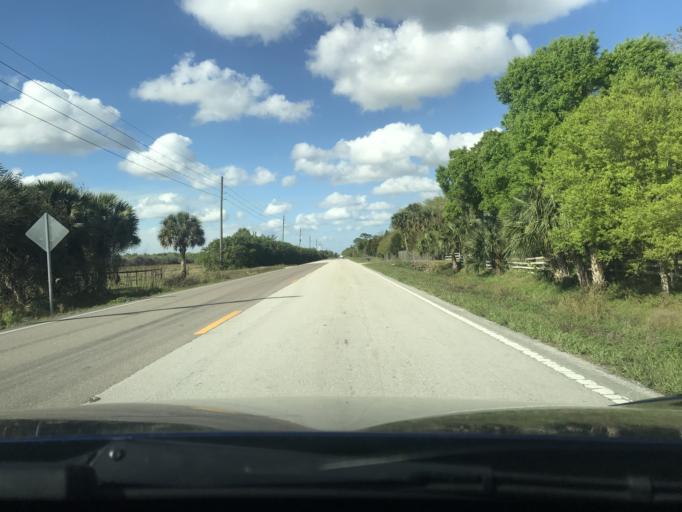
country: US
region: Florida
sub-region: Okeechobee County
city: Taylor Creek
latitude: 27.2146
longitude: -80.6941
